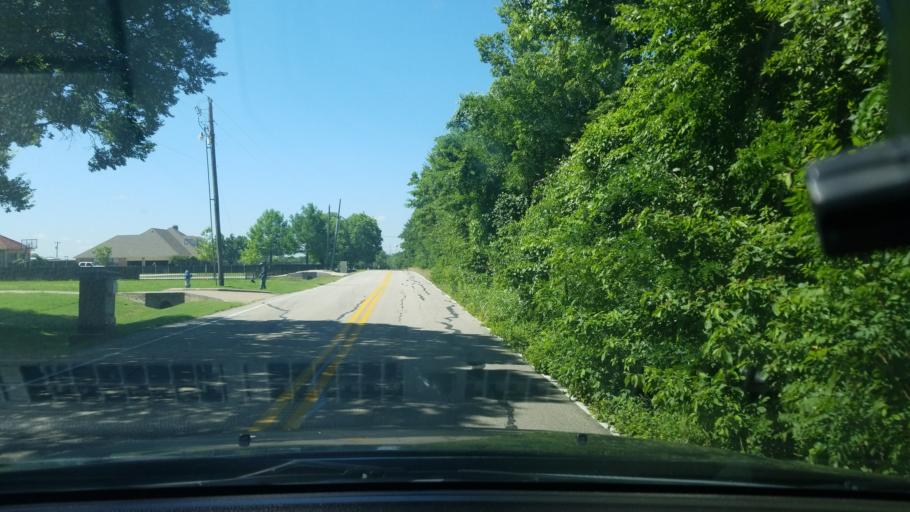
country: US
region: Texas
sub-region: Dallas County
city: Sunnyvale
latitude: 32.7863
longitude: -96.5550
